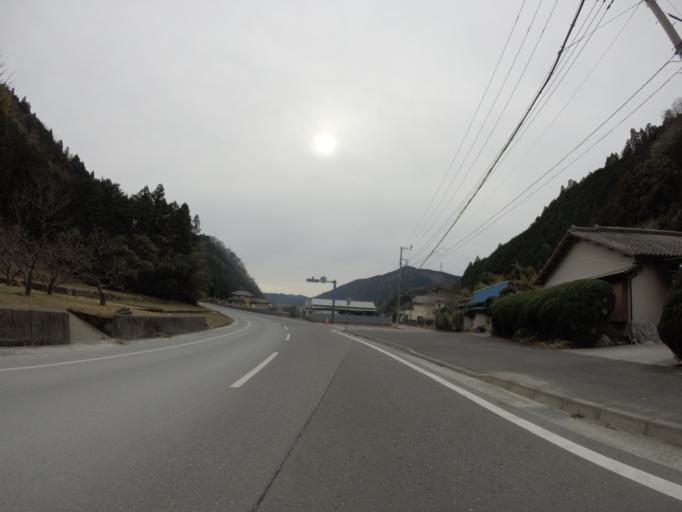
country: JP
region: Shizuoka
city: Fujinomiya
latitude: 35.2348
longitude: 138.5347
